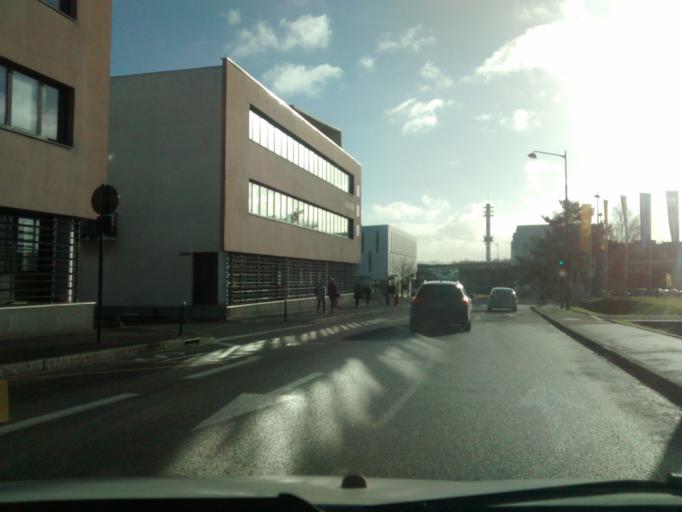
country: FR
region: Brittany
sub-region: Departement d'Ille-et-Vilaine
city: Cesson-Sevigne
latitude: 48.1324
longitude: -1.6361
